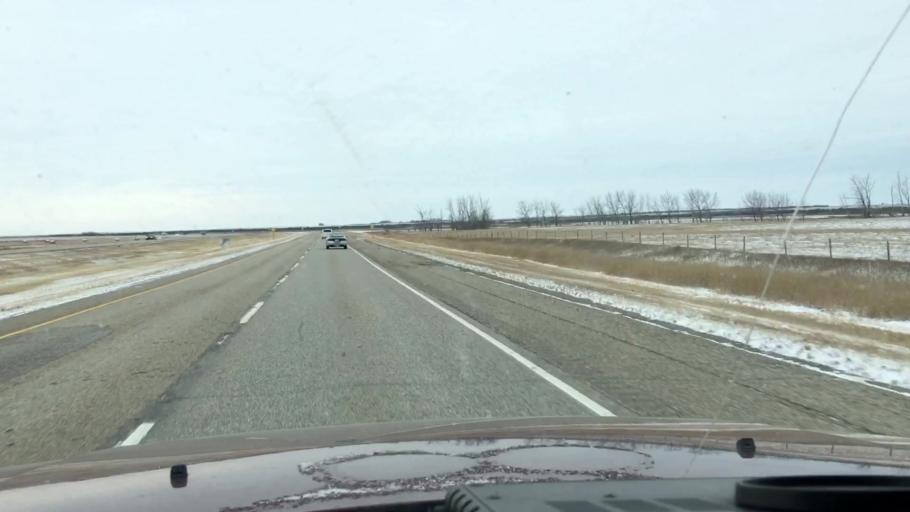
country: CA
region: Saskatchewan
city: Saskatoon
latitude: 51.4800
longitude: -106.2502
